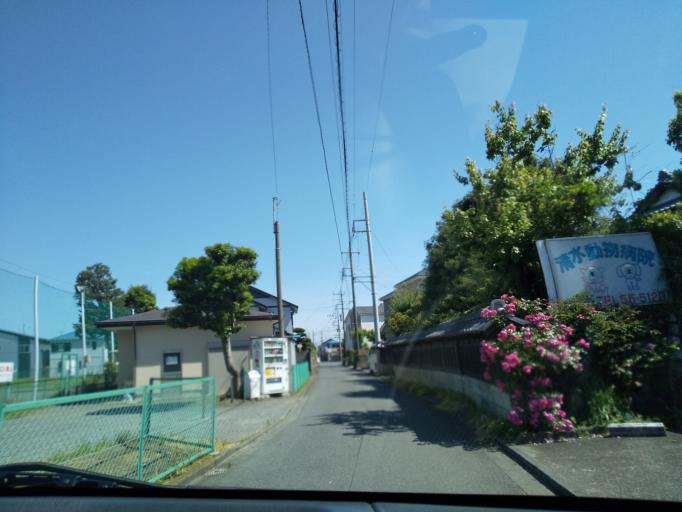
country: JP
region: Kanagawa
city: Zama
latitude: 35.5481
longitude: 139.3670
